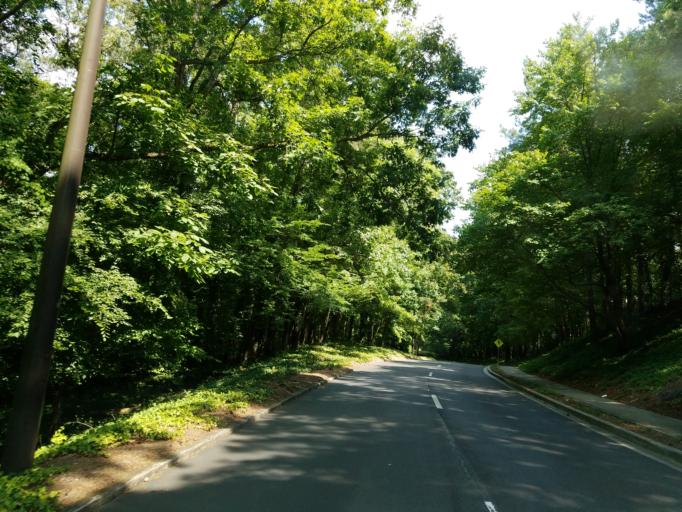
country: US
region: Georgia
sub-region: Cobb County
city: Smyrna
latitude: 33.8956
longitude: -84.4890
